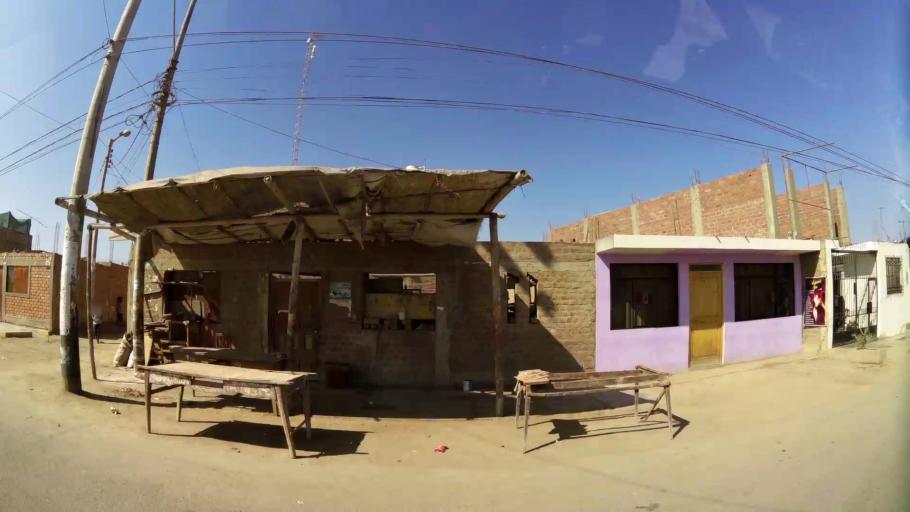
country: PE
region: Ica
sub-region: Provincia de Chincha
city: Sunampe
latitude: -13.4160
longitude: -76.1528
